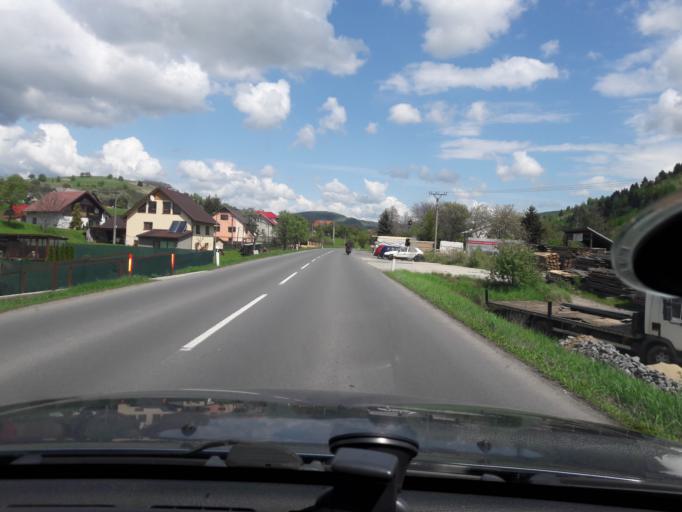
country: SK
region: Banskobystricky
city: Hrinova
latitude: 48.5665
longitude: 19.4961
